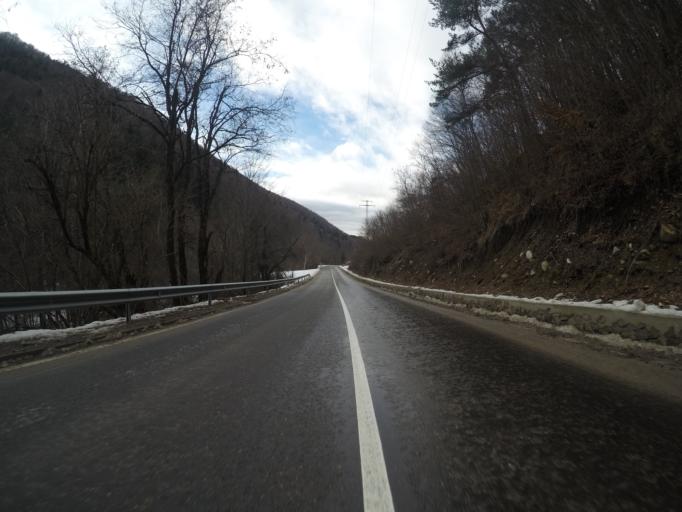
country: BG
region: Kyustendil
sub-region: Obshtina Rila
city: Rila
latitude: 42.1149
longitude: 23.3010
